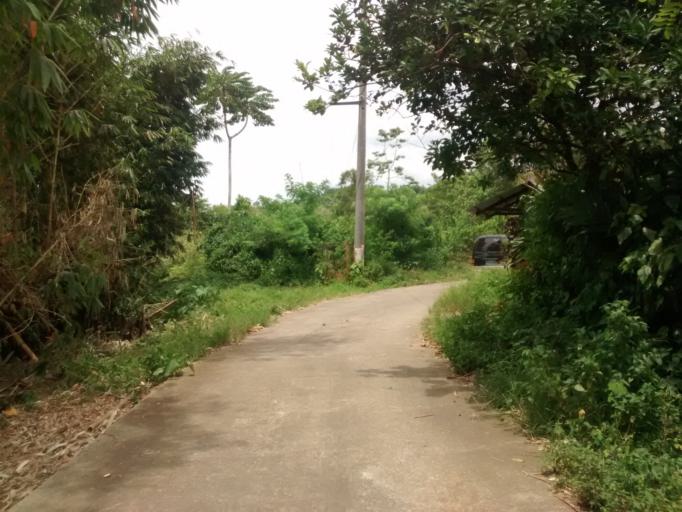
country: PH
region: Calabarzon
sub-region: Province of Quezon
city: Lucban
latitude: 14.1564
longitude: 121.5532
